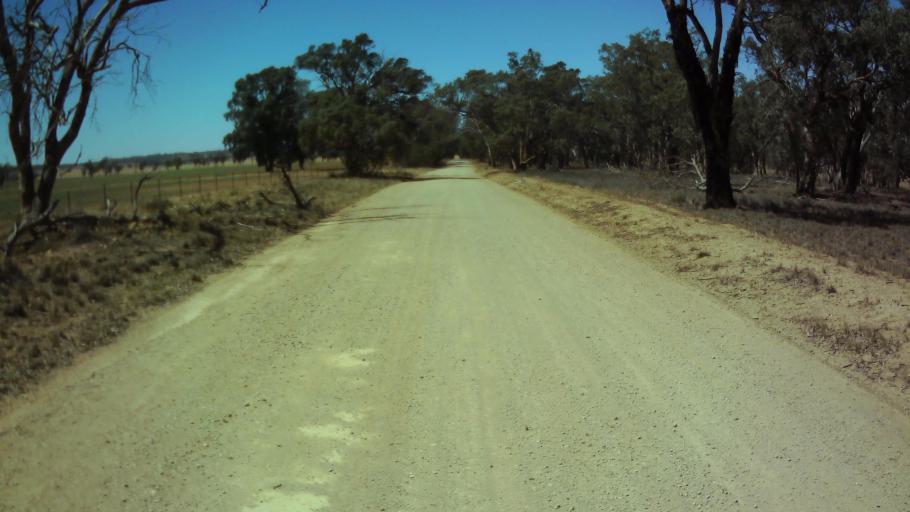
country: AU
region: New South Wales
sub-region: Weddin
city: Grenfell
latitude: -33.8796
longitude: 148.0886
